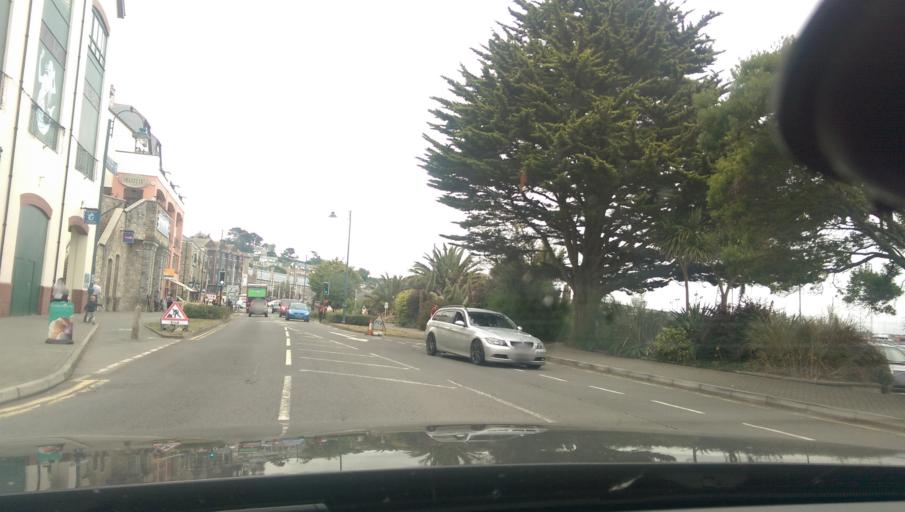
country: GB
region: England
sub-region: Cornwall
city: Penzance
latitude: 50.1197
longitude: -5.5332
